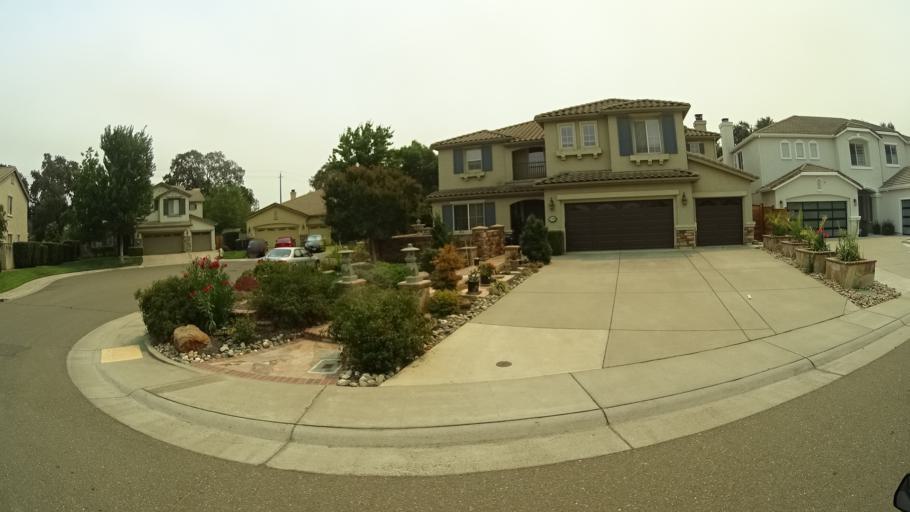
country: US
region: California
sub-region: Sacramento County
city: Laguna
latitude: 38.3986
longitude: -121.4188
